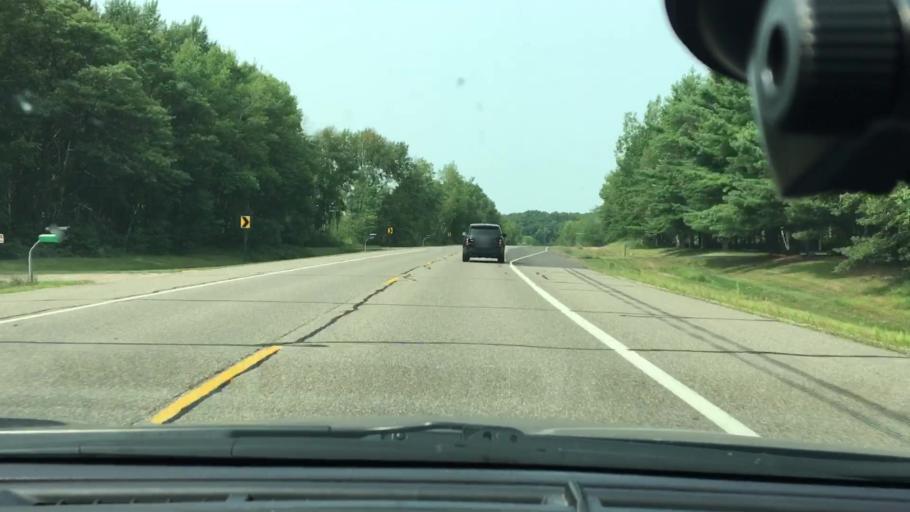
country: US
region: Minnesota
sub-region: Crow Wing County
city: Baxter
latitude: 46.3837
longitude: -94.3057
